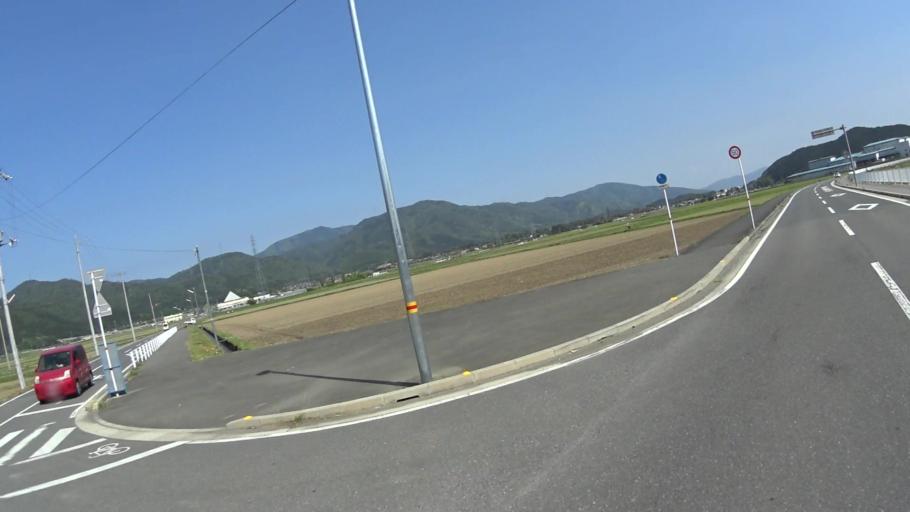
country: JP
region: Kyoto
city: Kameoka
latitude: 35.0914
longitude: 135.5364
